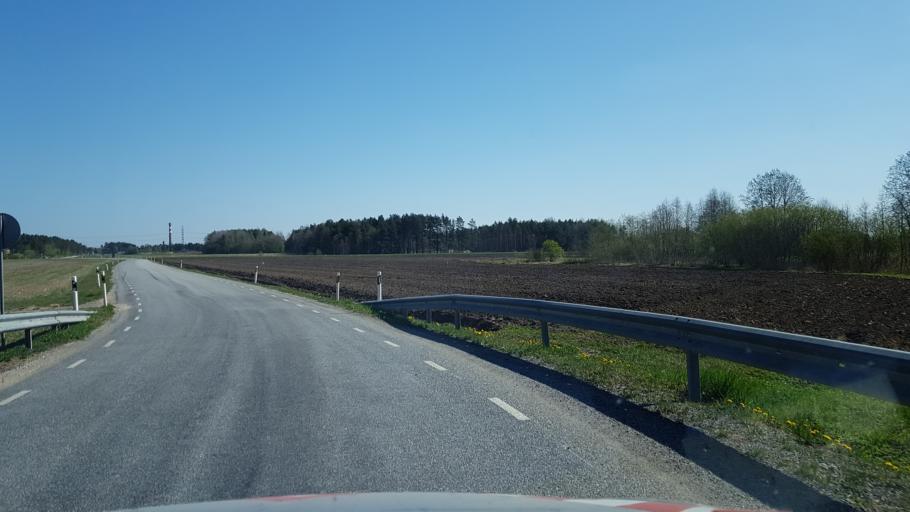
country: EE
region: Harju
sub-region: Saue vald
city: Laagri
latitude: 59.3381
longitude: 24.5835
